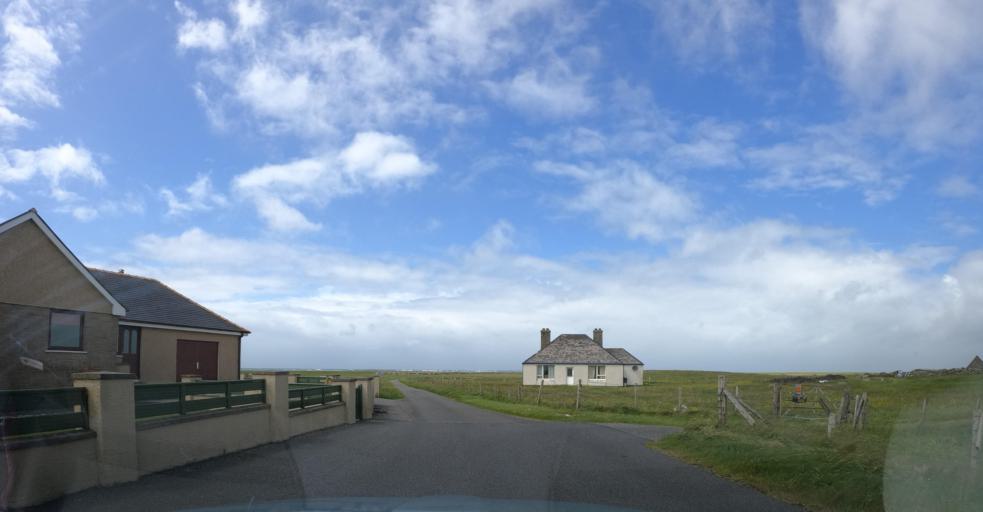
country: GB
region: Scotland
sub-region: Eilean Siar
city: Isle of South Uist
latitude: 57.2795
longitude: -7.4155
